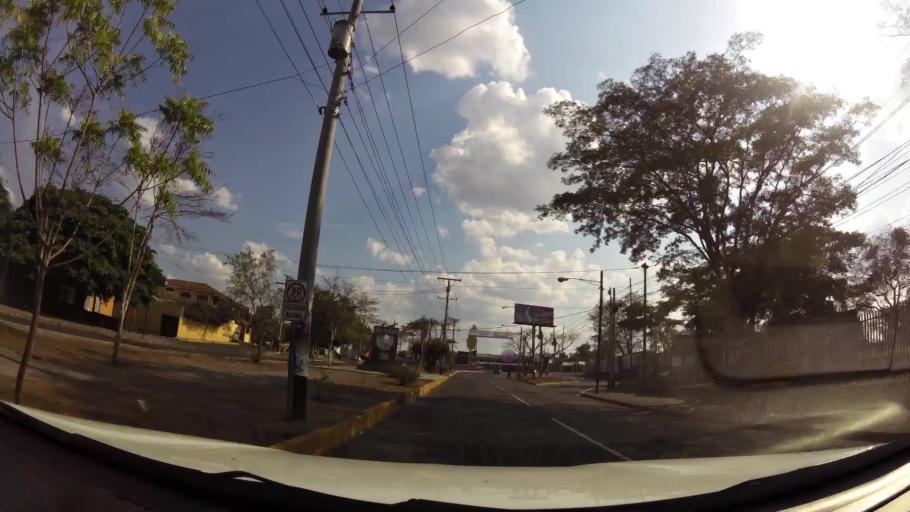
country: NI
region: Managua
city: Managua
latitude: 12.1266
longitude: -86.2825
